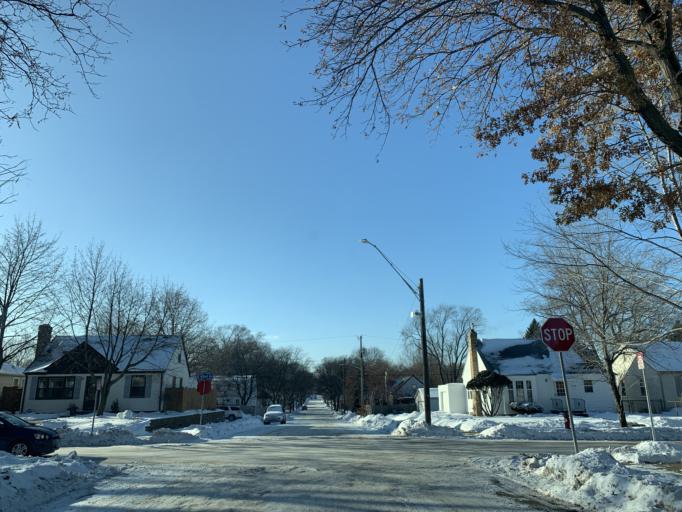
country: US
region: Minnesota
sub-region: Hennepin County
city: Richfield
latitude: 44.8999
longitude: -93.2125
